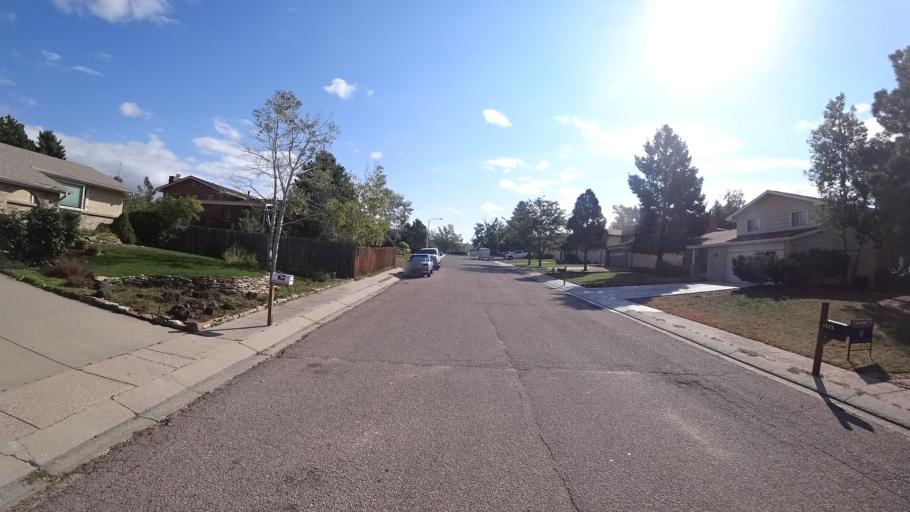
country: US
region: Colorado
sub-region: El Paso County
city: Cimarron Hills
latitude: 38.8828
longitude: -104.7300
